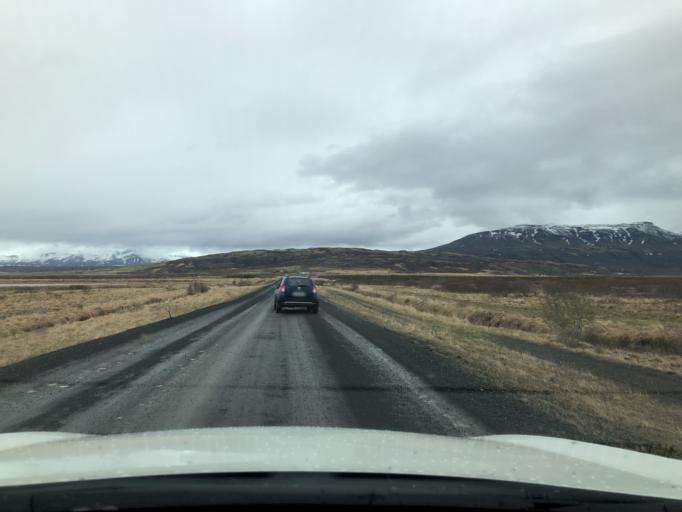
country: IS
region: South
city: Selfoss
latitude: 64.2592
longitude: -20.3325
